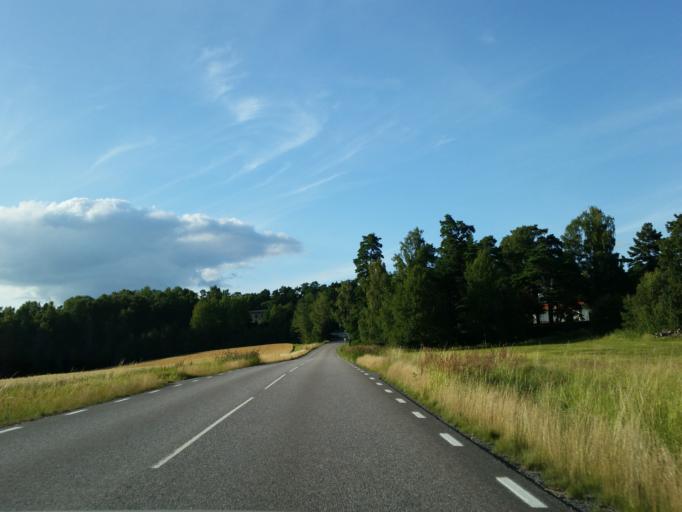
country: SE
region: Soedermanland
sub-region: Gnesta Kommun
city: Gnesta
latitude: 59.0266
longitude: 17.3585
